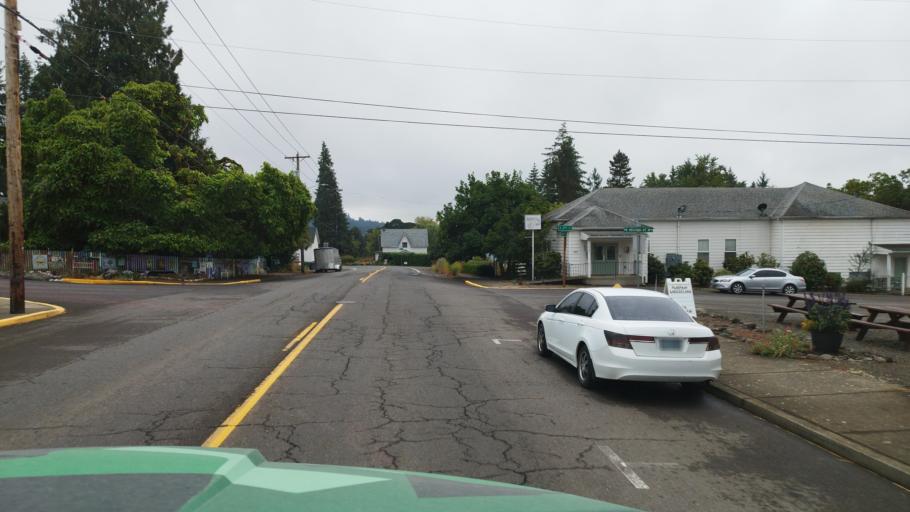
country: US
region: Oregon
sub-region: Yamhill County
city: Yamhill
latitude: 45.3403
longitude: -123.1879
